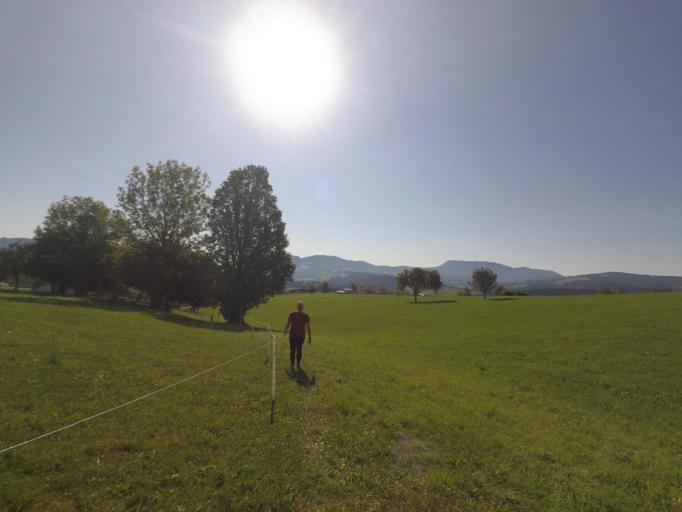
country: AT
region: Styria
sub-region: Politischer Bezirk Weiz
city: Passail
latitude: 47.2884
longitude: 15.4724
